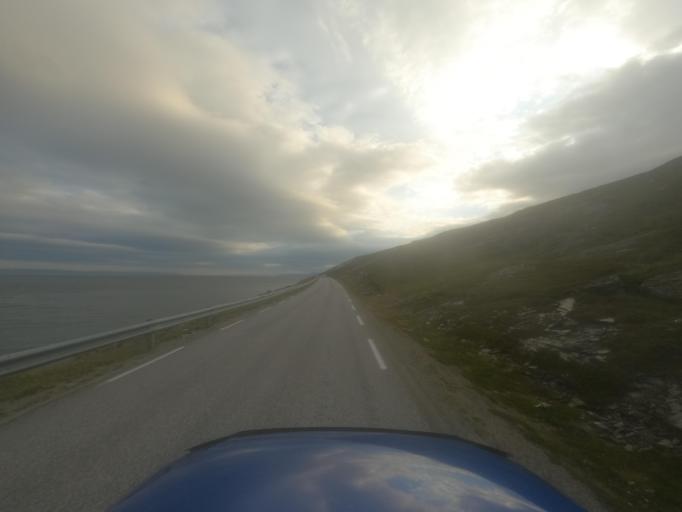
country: NO
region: Finnmark Fylke
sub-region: Nordkapp
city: Honningsvag
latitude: 70.7148
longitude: 25.5694
